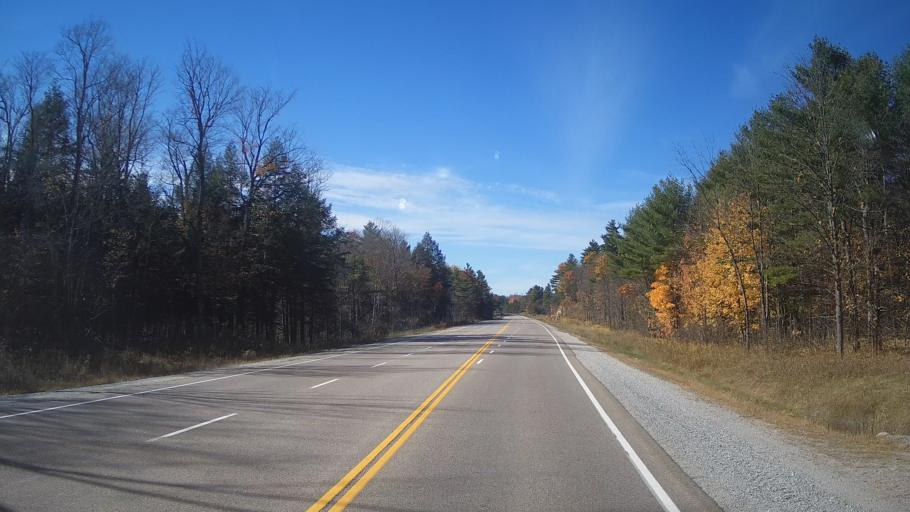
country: CA
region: Ontario
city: Perth
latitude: 44.8508
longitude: -76.4598
